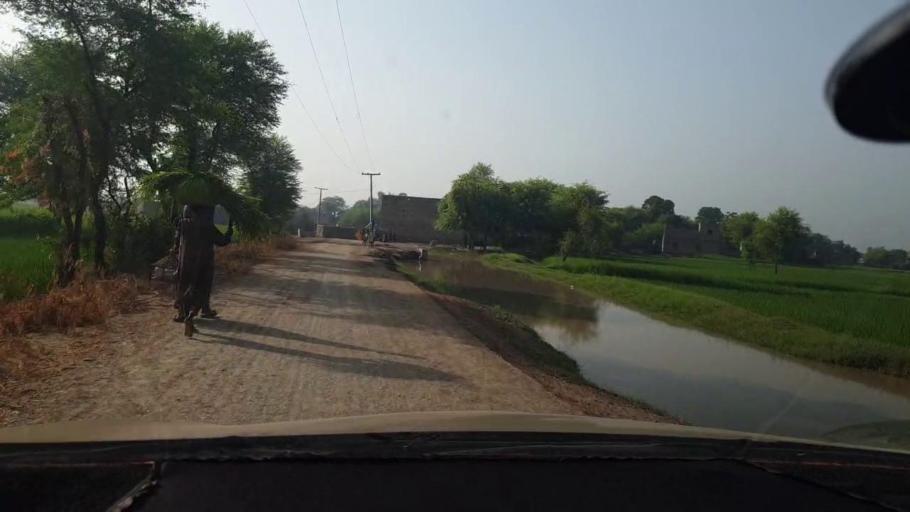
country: PK
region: Sindh
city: Kambar
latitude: 27.5361
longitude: 68.0188
